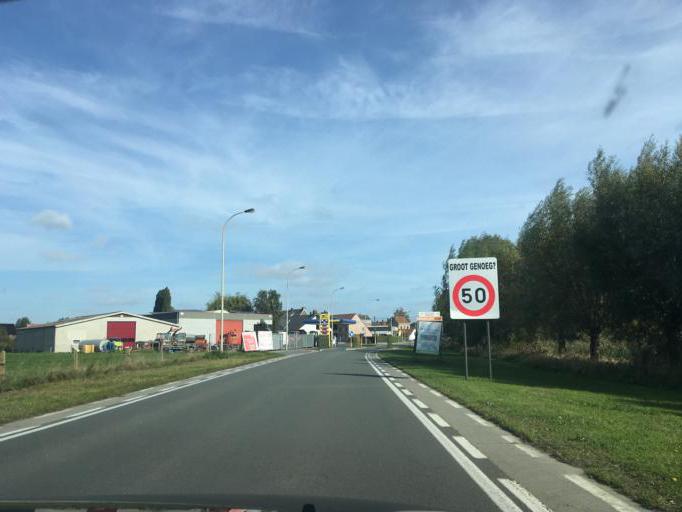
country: BE
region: Flanders
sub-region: Provincie West-Vlaanderen
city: Roeselare
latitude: 50.9283
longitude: 3.0910
